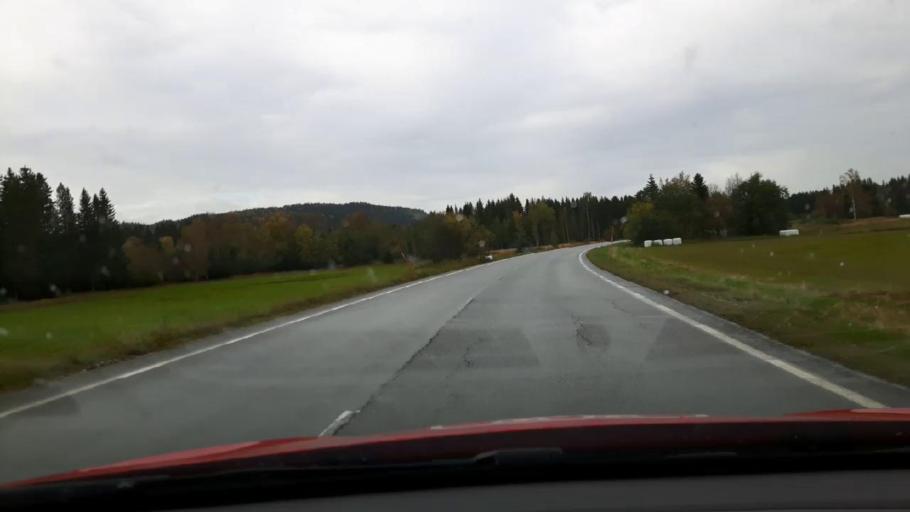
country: SE
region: Jaemtland
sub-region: Bergs Kommun
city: Hoverberg
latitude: 62.9054
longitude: 14.3351
